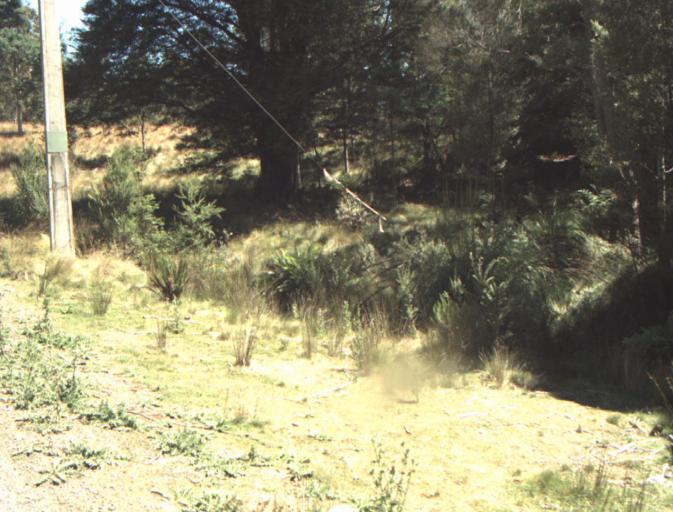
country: AU
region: Tasmania
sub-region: Dorset
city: Scottsdale
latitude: -41.3597
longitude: 147.4163
